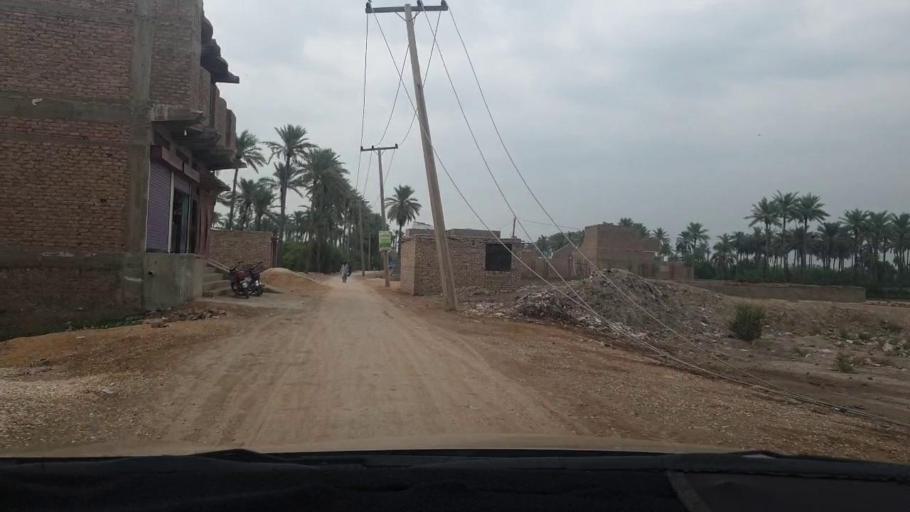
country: PK
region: Sindh
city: Larkana
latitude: 27.5688
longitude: 68.2273
